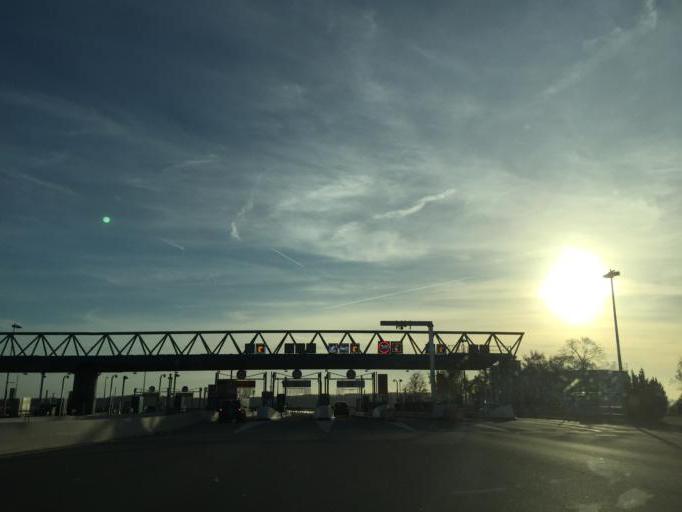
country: FR
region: Rhone-Alpes
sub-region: Departement du Rhone
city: Saint-Laurent-de-Mure
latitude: 45.6734
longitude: 5.0517
